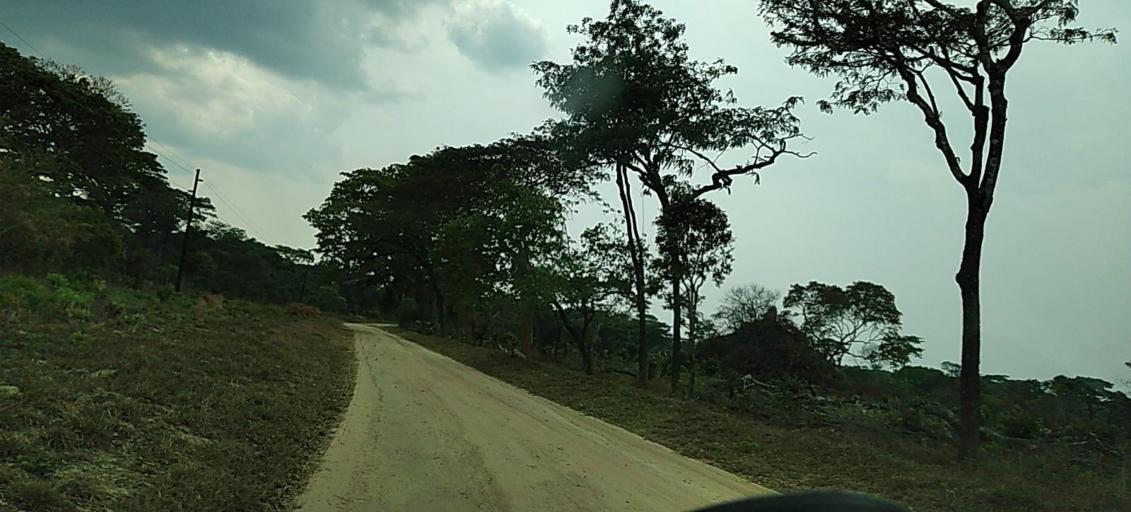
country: ZM
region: North-Western
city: Solwezi
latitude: -12.7704
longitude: 26.4662
